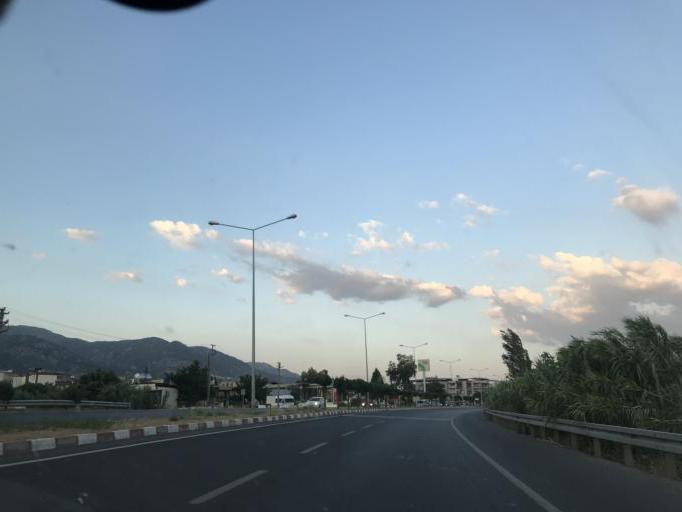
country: TR
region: Aydin
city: Buharkent
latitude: 37.9632
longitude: 28.7314
